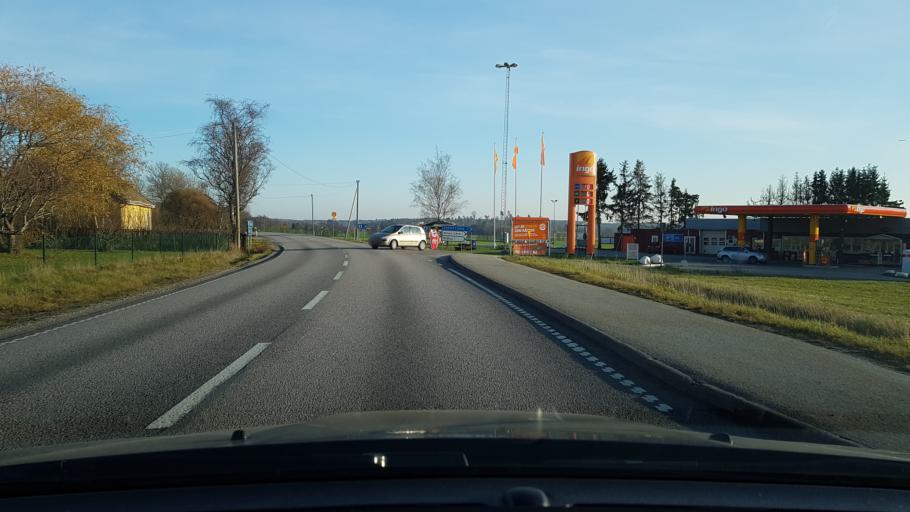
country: SE
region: Stockholm
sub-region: Norrtalje Kommun
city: Nykvarn
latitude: 59.7392
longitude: 18.1601
